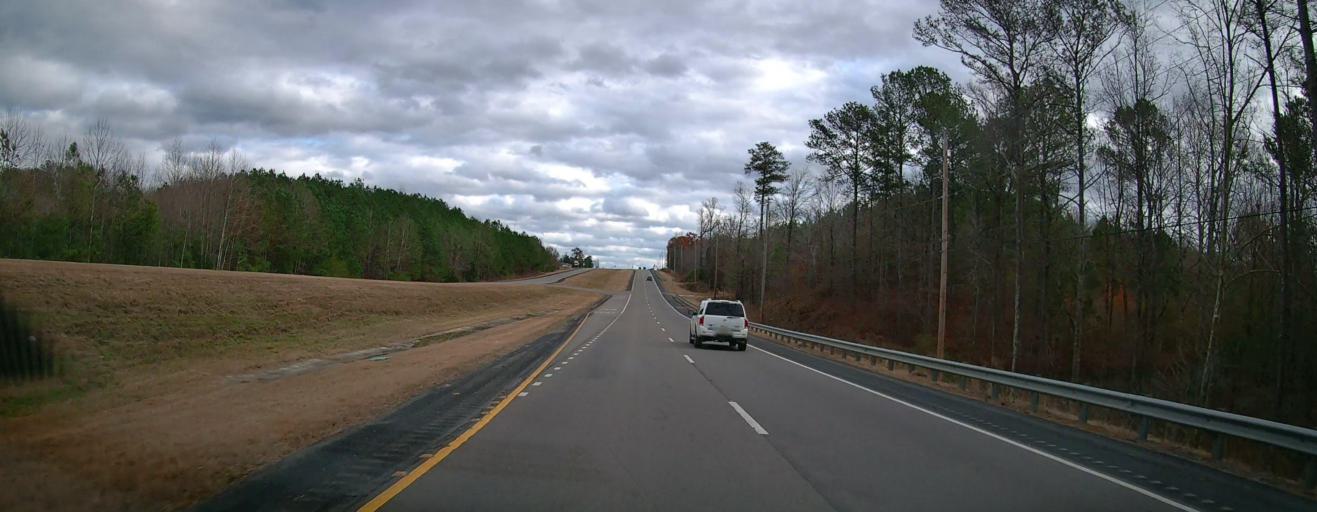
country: US
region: Alabama
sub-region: Morgan County
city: Falkville
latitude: 34.2489
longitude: -86.9666
